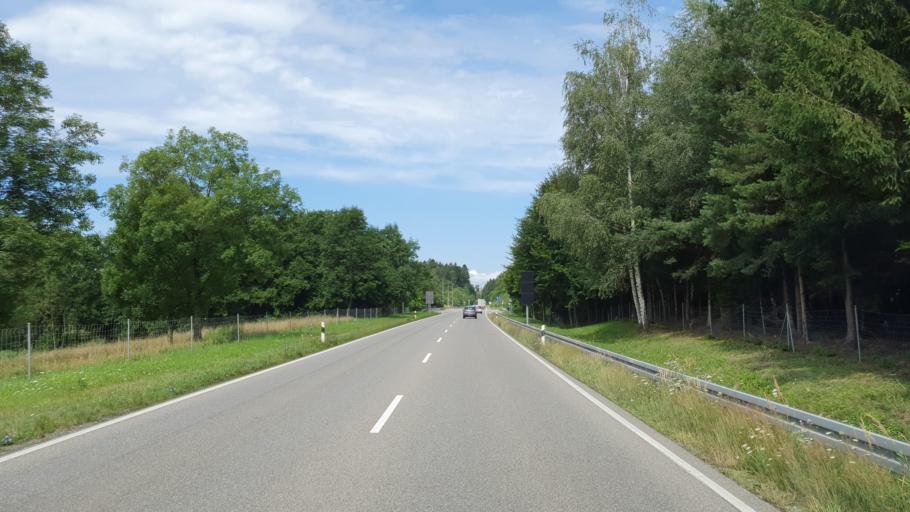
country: DE
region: Bavaria
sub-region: Swabia
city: Bodolz
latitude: 47.5890
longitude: 9.6493
